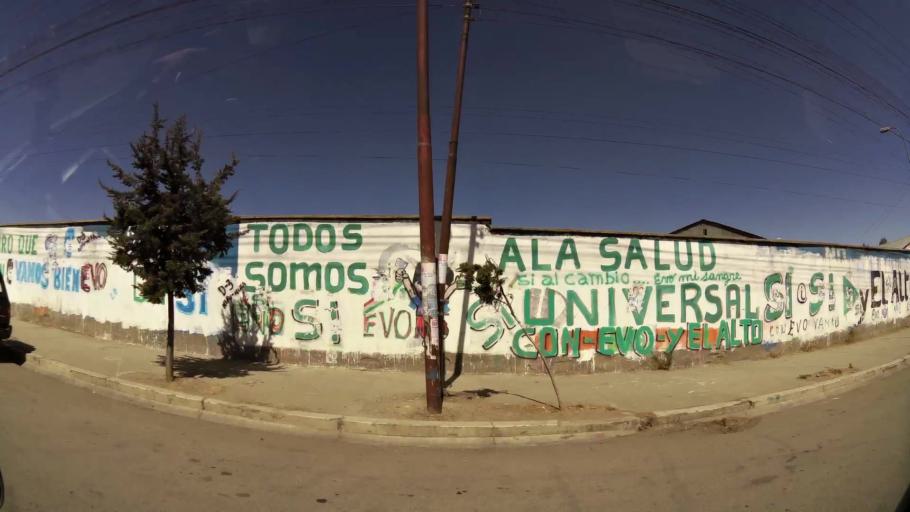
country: BO
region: La Paz
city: La Paz
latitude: -16.4996
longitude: -68.1765
